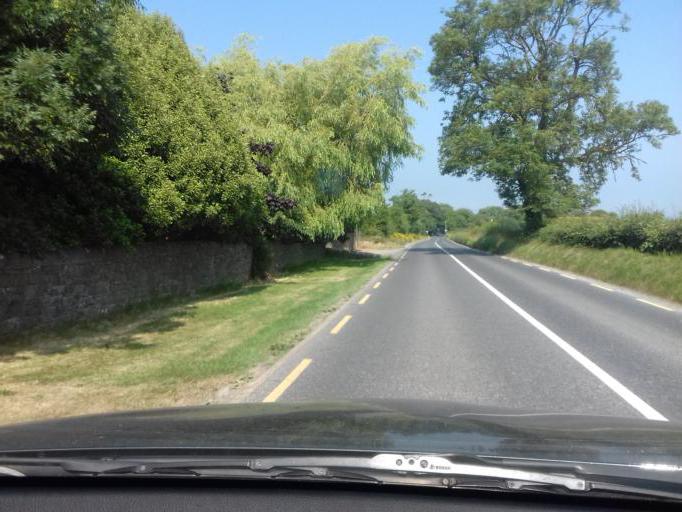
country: IE
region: Leinster
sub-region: An Mhi
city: Stamullin
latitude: 53.5908
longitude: -6.2769
